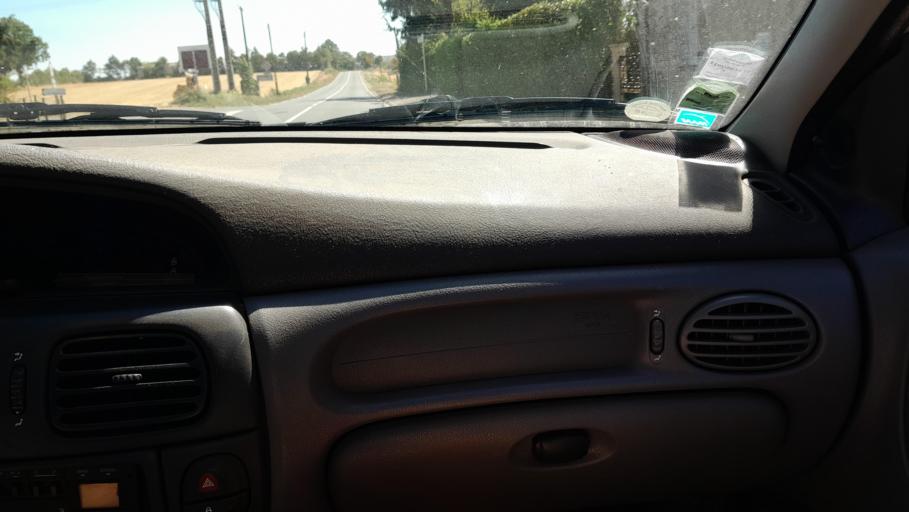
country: FR
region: Pays de la Loire
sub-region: Departement de la Loire-Atlantique
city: Saint-Mars-la-Jaille
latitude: 47.6188
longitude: -1.1985
